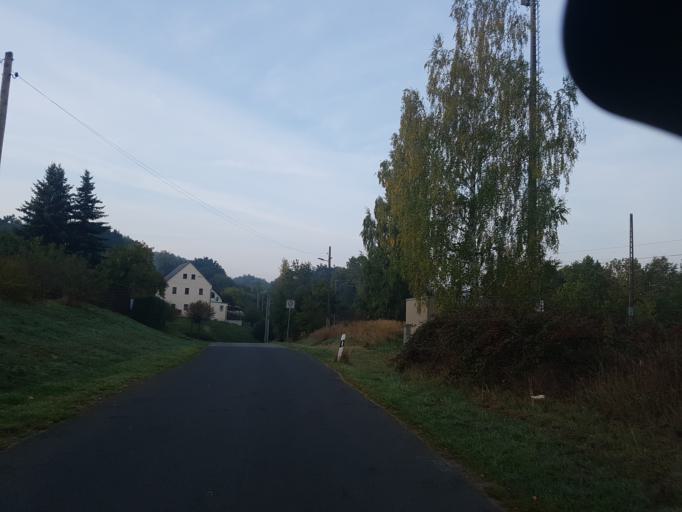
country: DE
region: Saxony
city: Grossweitzschen
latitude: 51.1166
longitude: 13.0493
